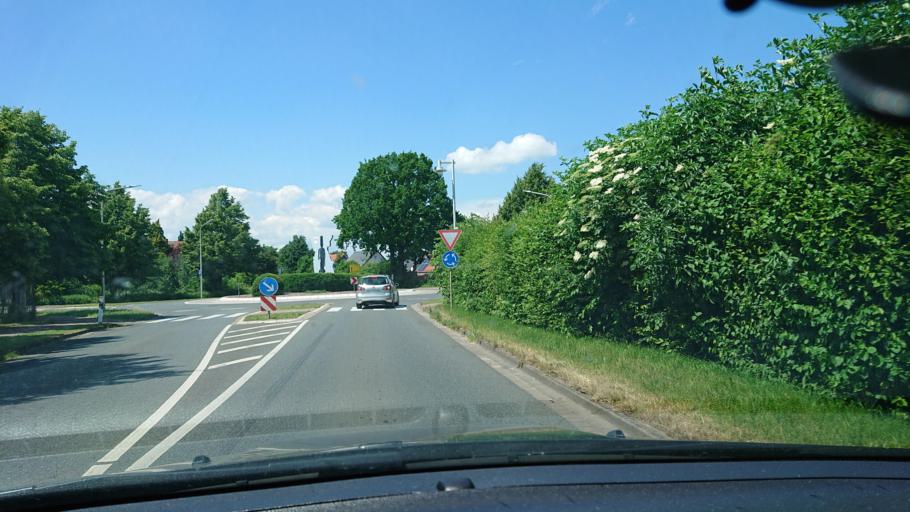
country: DE
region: North Rhine-Westphalia
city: Preussisch Oldendorf
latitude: 52.3076
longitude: 8.4866
